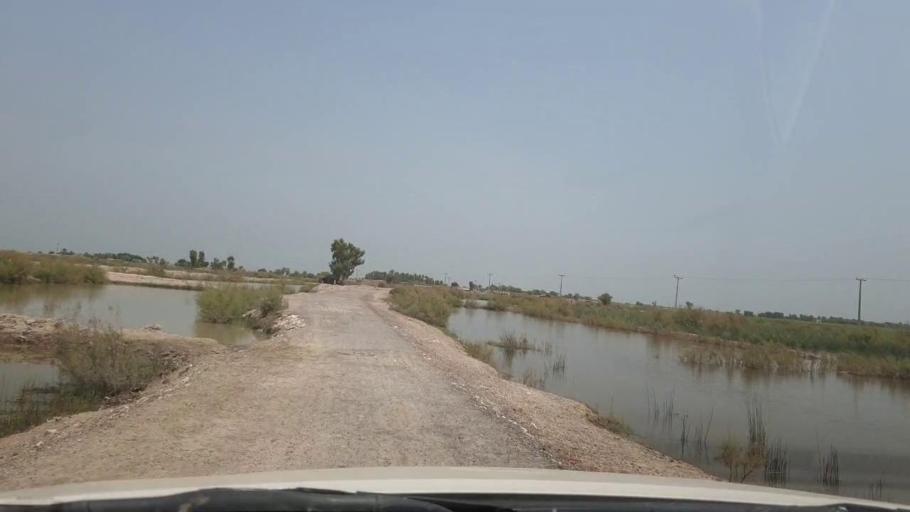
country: PK
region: Sindh
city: Rustam jo Goth
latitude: 28.0235
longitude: 68.7865
